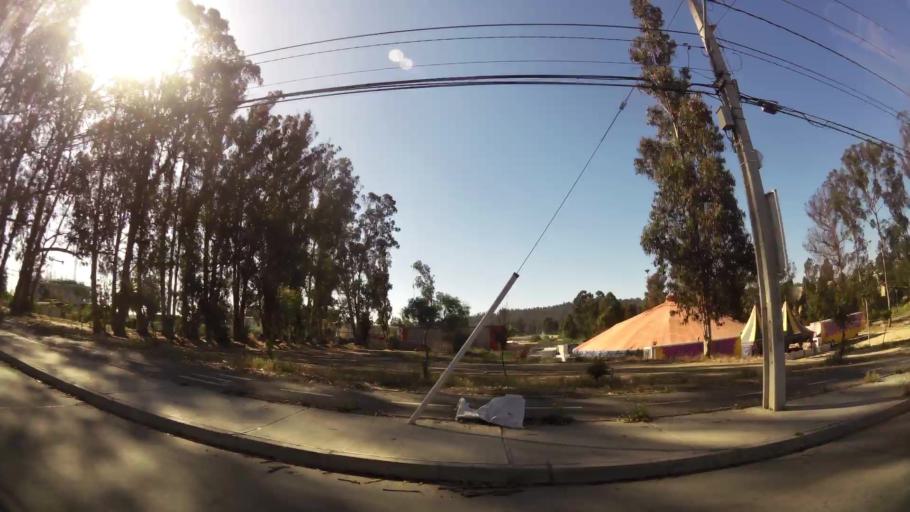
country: CL
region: Valparaiso
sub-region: Provincia de Valparaiso
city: Valparaiso
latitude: -33.1195
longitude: -71.5732
